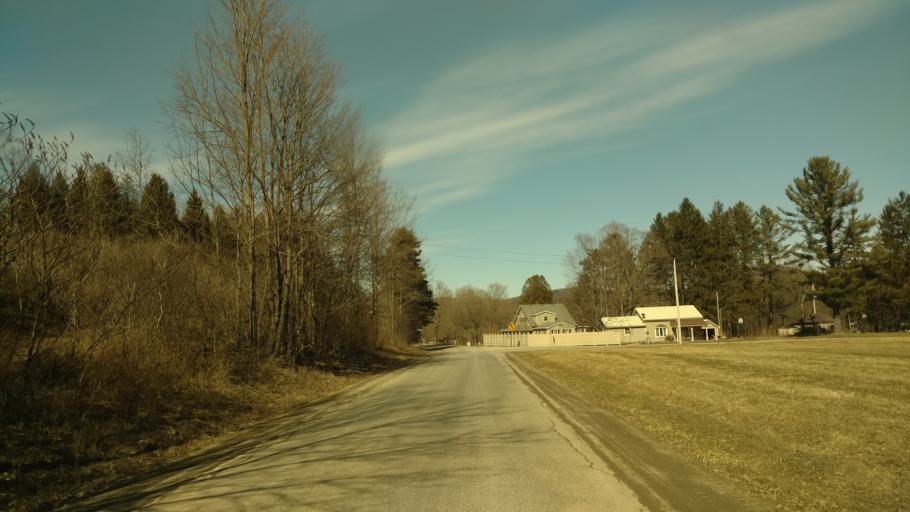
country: US
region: New York
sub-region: Allegany County
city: Wellsville
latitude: 42.0704
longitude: -77.9270
